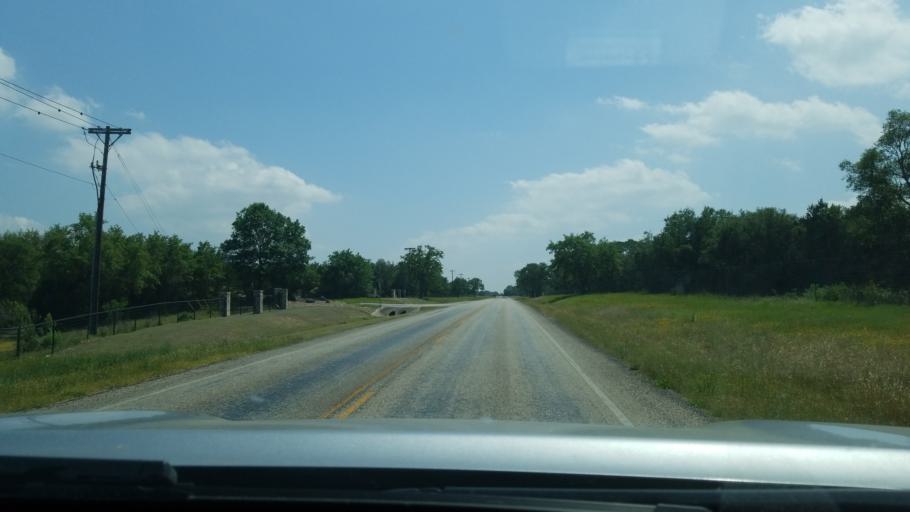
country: US
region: Texas
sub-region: Bexar County
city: Fair Oaks Ranch
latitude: 29.8834
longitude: -98.5568
